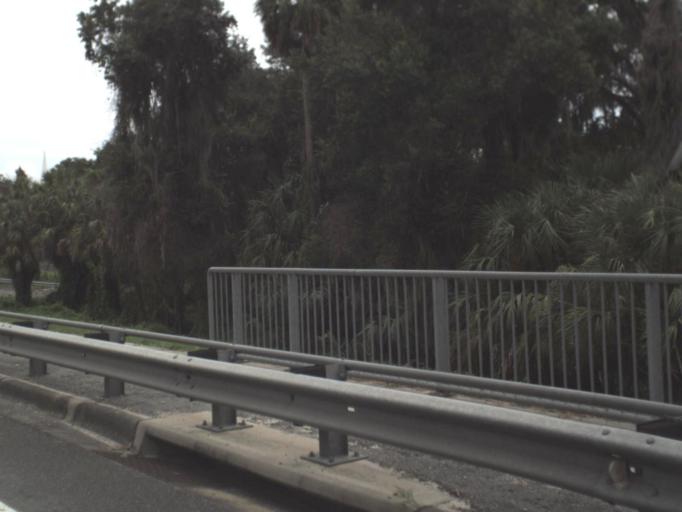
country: US
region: Florida
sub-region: Citrus County
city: Inverness
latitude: 28.8333
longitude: -82.3229
